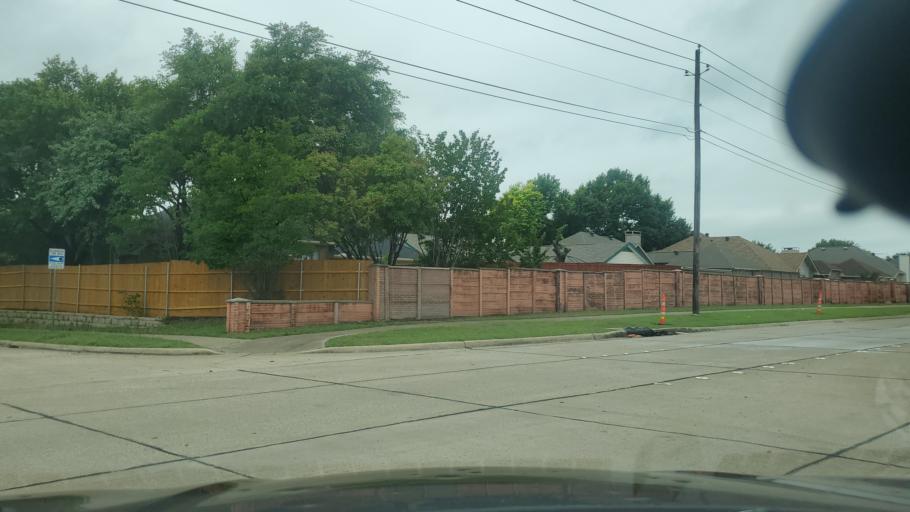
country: US
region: Texas
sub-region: Dallas County
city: Garland
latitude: 32.9554
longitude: -96.6584
